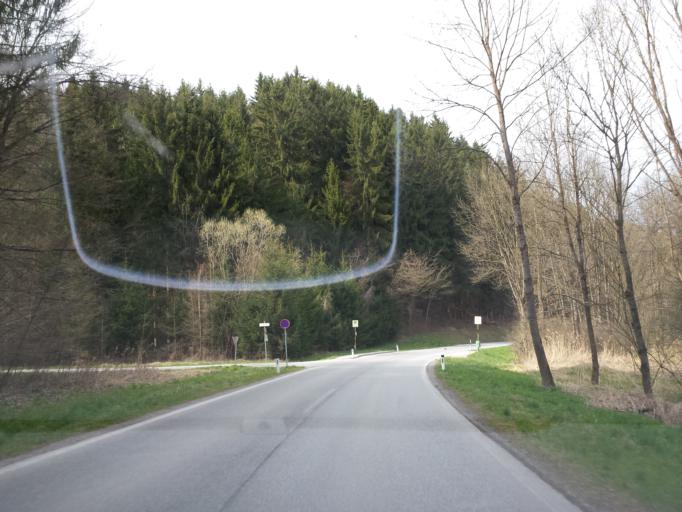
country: AT
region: Styria
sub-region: Politischer Bezirk Graz-Umgebung
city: Thal
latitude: 47.0745
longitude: 15.3642
